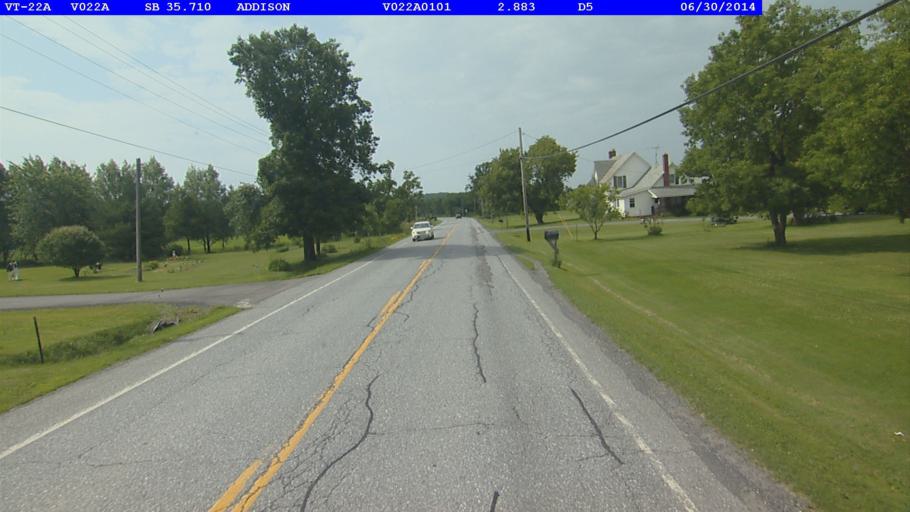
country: US
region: Vermont
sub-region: Addison County
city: Vergennes
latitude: 44.0710
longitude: -73.3042
